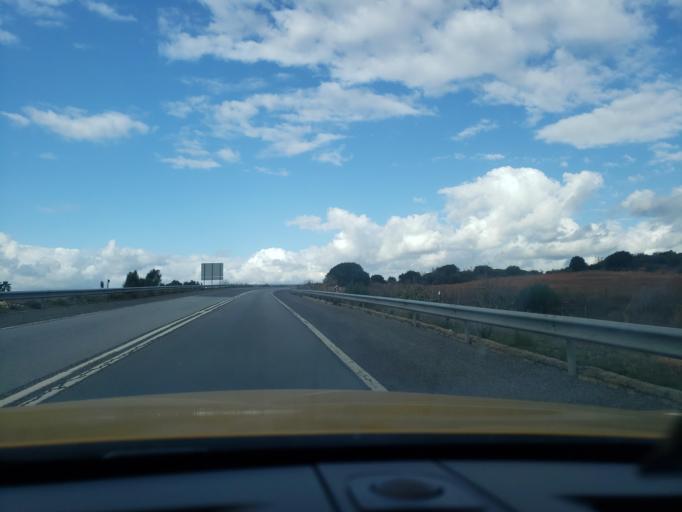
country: PT
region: Faro
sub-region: Portimao
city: Alvor
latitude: 37.1645
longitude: -8.5698
